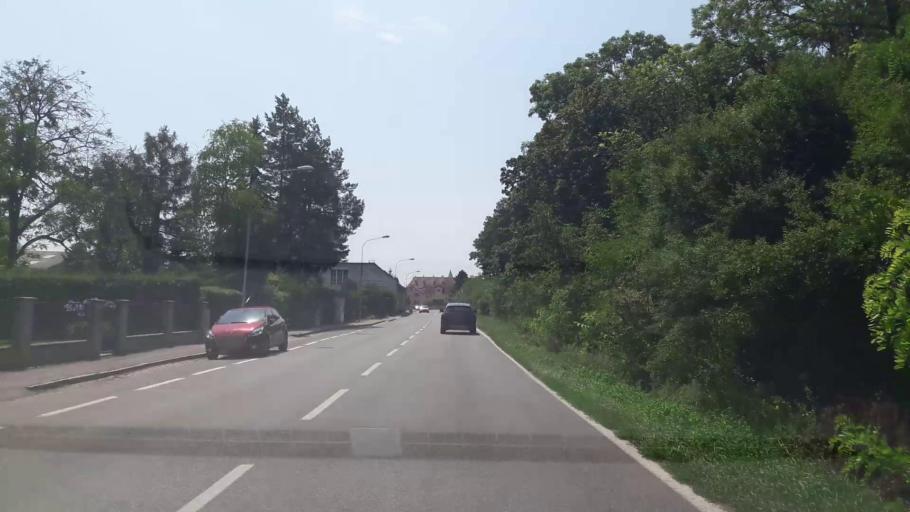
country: AT
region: Lower Austria
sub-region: Politischer Bezirk Wien-Umgebung
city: Schwadorf
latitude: 48.0535
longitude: 16.6078
